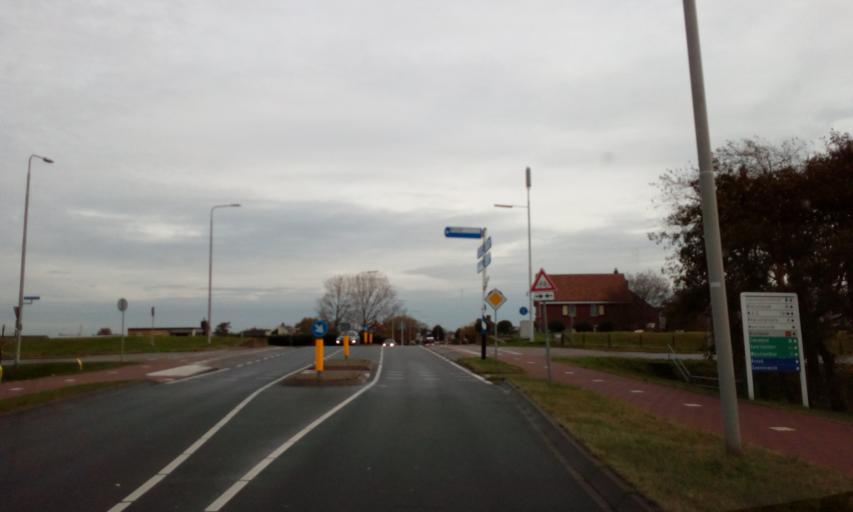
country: NL
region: South Holland
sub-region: Gemeente Westland
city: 's-Gravenzande
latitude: 52.0033
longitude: 4.1513
